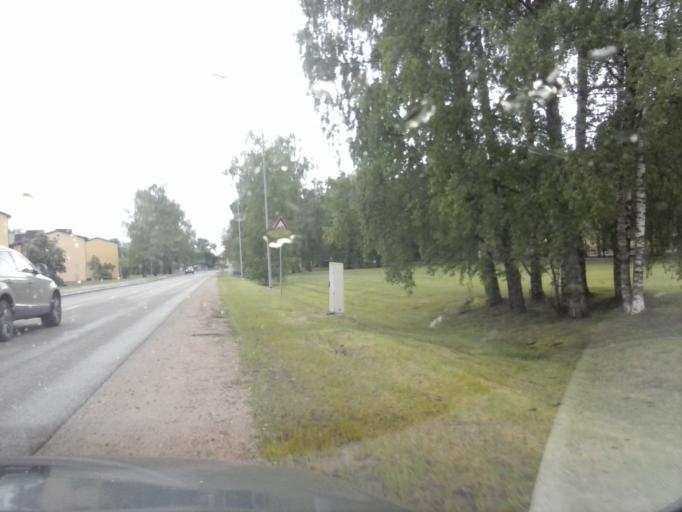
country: LV
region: Valmieras Rajons
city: Valmiera
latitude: 57.5516
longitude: 25.4356
